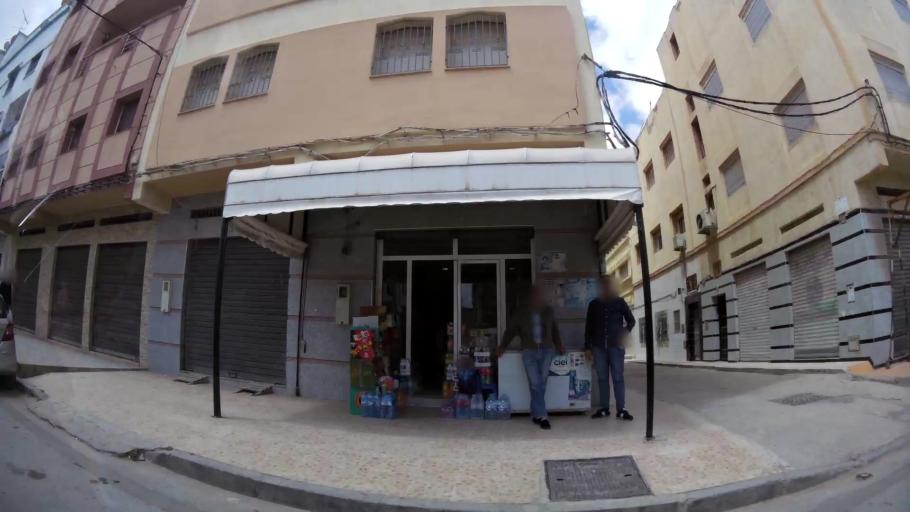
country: MA
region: Oriental
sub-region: Nador
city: Nador
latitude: 35.1717
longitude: -2.9199
